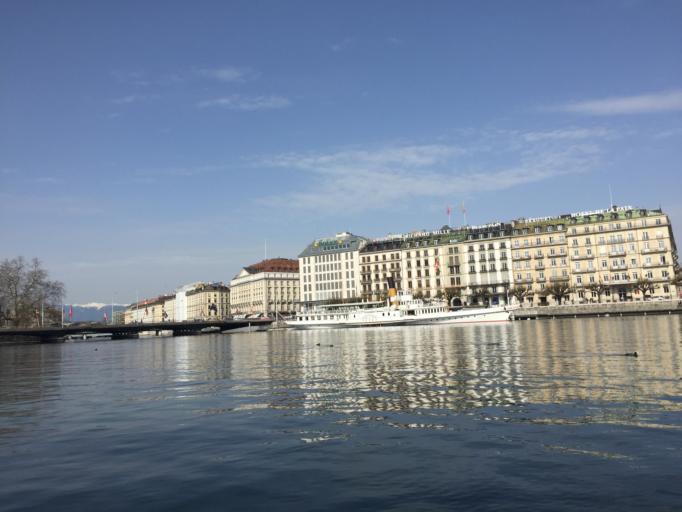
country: CH
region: Geneva
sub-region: Geneva
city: Geneve
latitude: 46.2070
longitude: 6.1506
